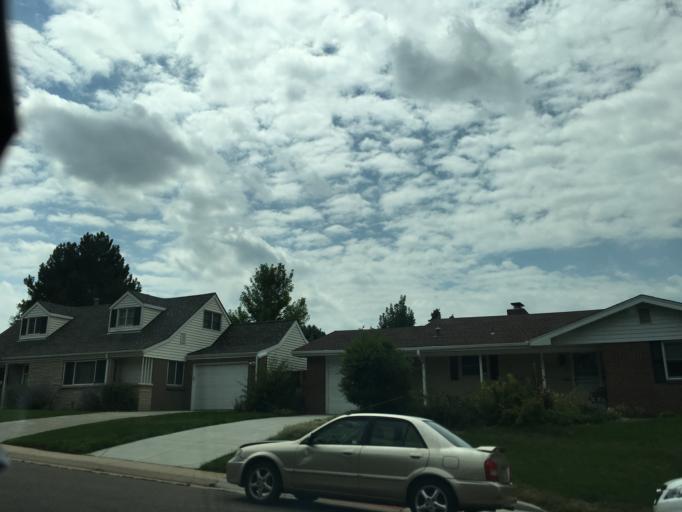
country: US
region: Colorado
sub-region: Arapahoe County
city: Sheridan
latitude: 39.6644
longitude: -105.0363
